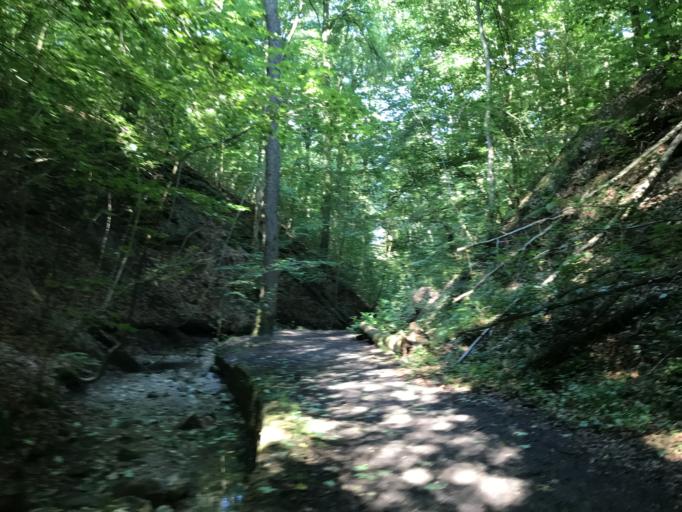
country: DE
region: Baden-Wuerttemberg
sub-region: Regierungsbezirk Stuttgart
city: Stuttgart
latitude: 48.7476
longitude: 9.1431
